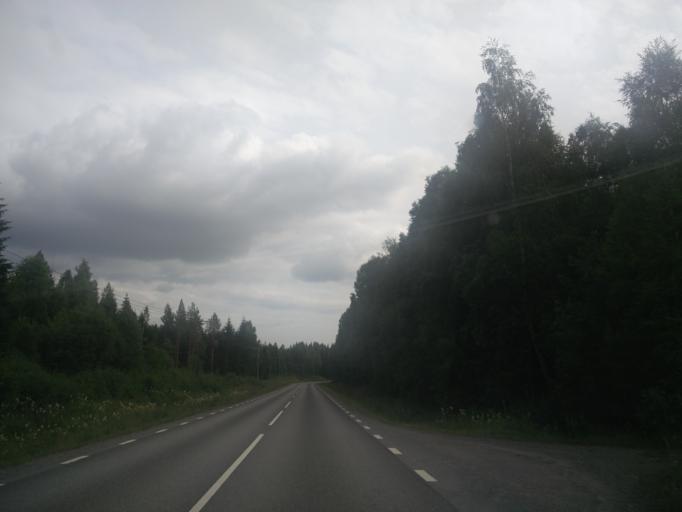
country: SE
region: Vaermland
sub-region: Arvika Kommun
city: Arvika
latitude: 59.7251
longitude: 12.5667
